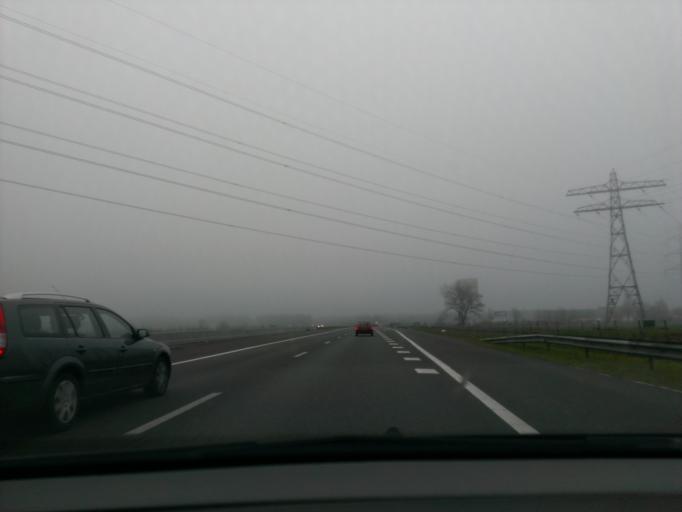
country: NL
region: Drenthe
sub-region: Gemeente Hoogeveen
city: Hoogeveen
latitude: 52.7323
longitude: 6.4651
